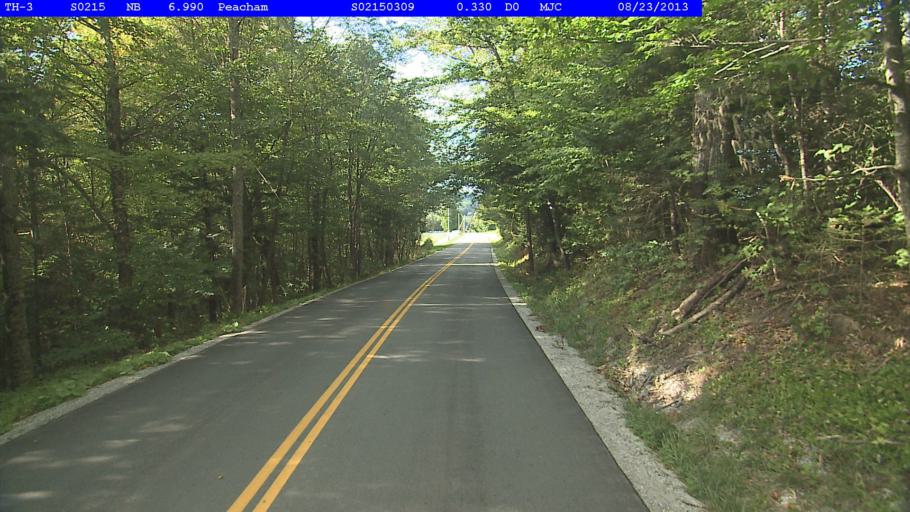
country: US
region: Vermont
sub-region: Caledonia County
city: Saint Johnsbury
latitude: 44.3026
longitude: -72.1643
